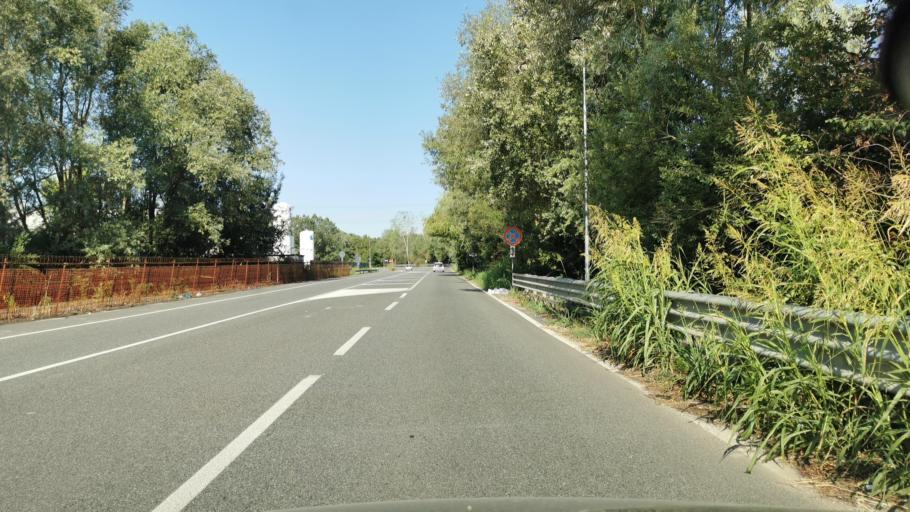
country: IT
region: Piedmont
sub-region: Provincia di Torino
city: Settimo Torinese
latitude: 45.1600
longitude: 7.7625
